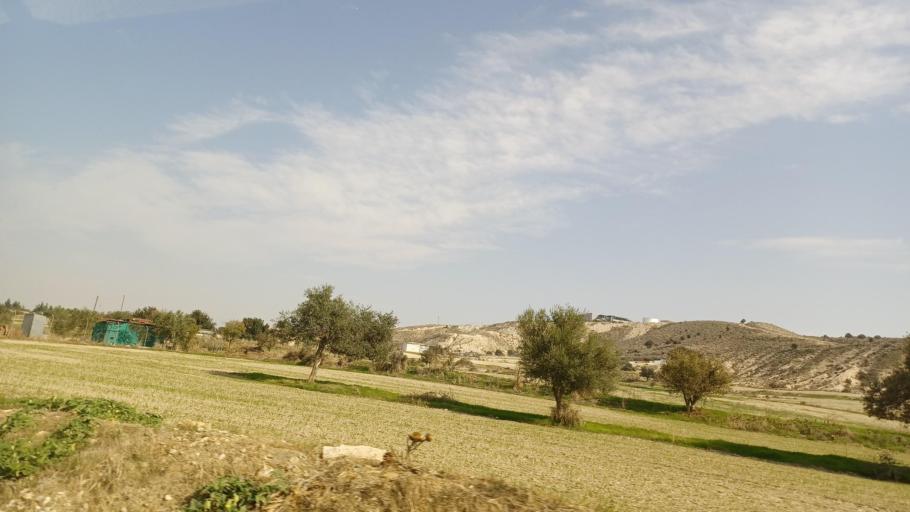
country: CY
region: Lefkosia
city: Lympia
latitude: 34.9843
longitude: 33.4551
